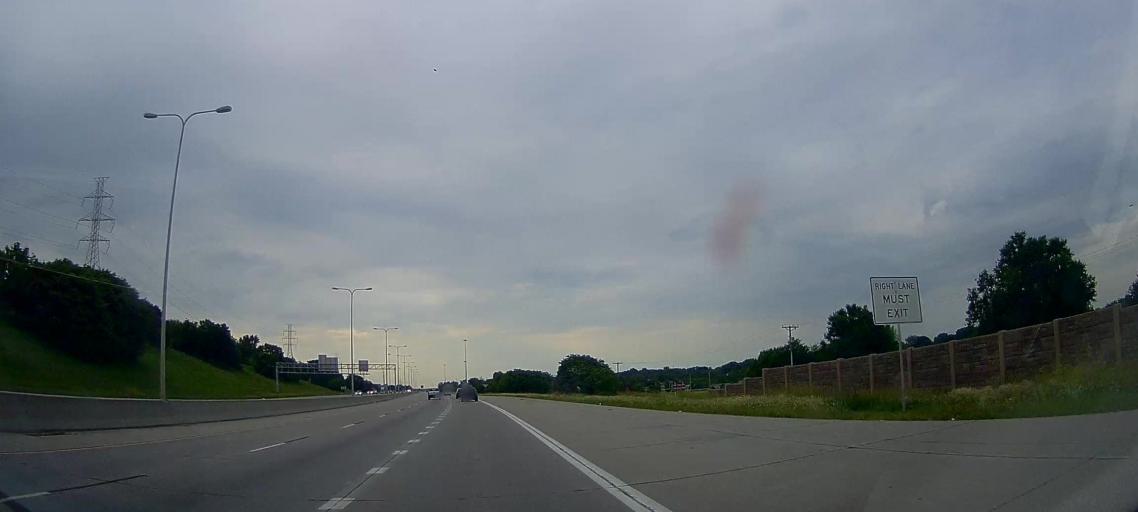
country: US
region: Nebraska
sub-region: Douglas County
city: Ralston
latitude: 41.2989
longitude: -96.0710
